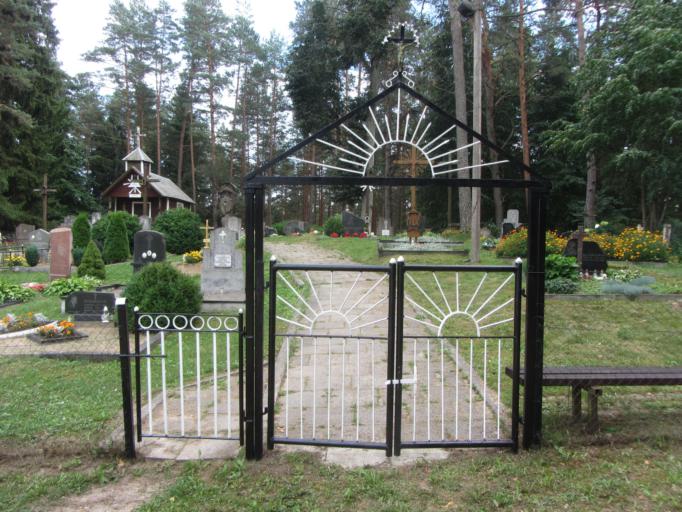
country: LT
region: Alytaus apskritis
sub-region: Alytaus rajonas
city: Daugai
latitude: 54.2016
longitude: 24.1813
